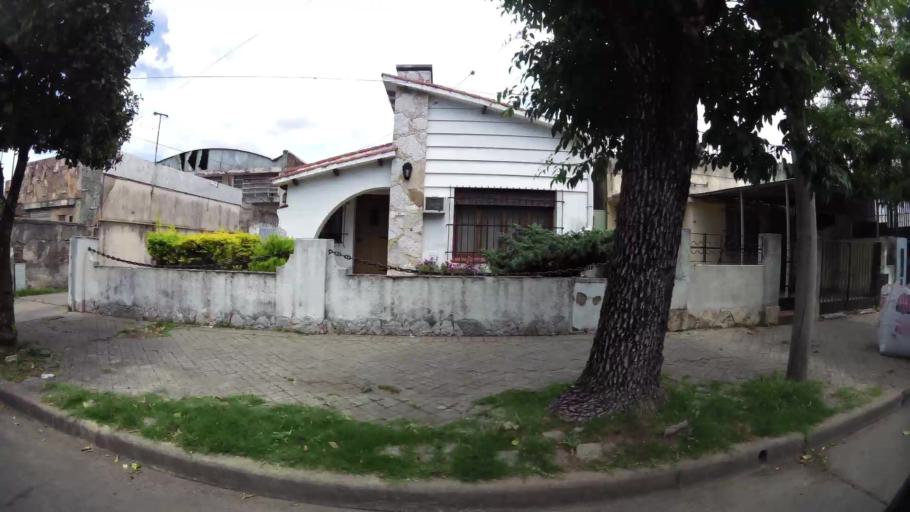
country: AR
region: Santa Fe
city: Gobernador Galvez
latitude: -32.9973
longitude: -60.6308
